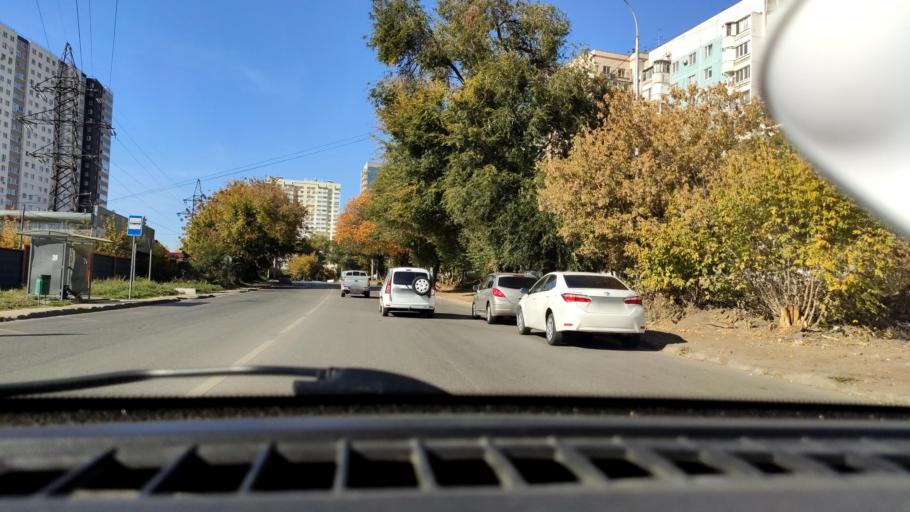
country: RU
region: Samara
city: Samara
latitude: 53.1866
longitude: 50.1392
